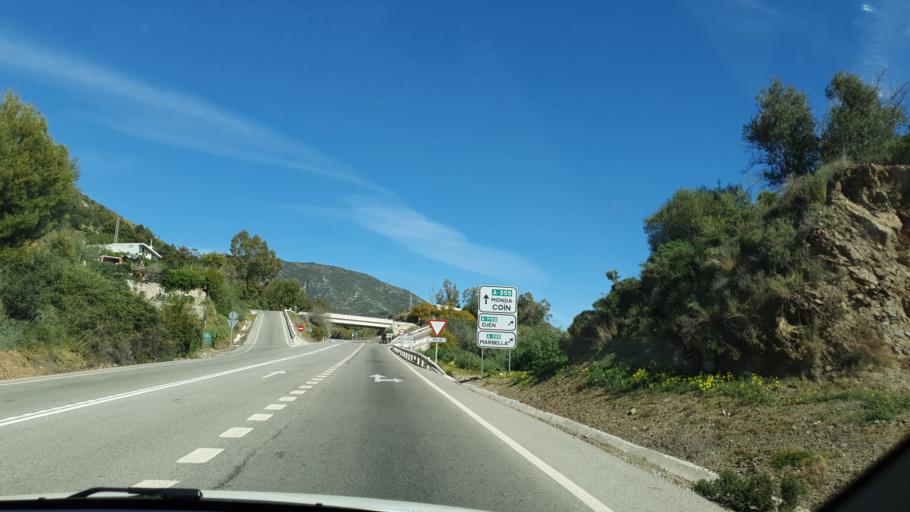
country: ES
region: Andalusia
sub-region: Provincia de Malaga
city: Ojen
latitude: 36.5462
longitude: -4.8614
